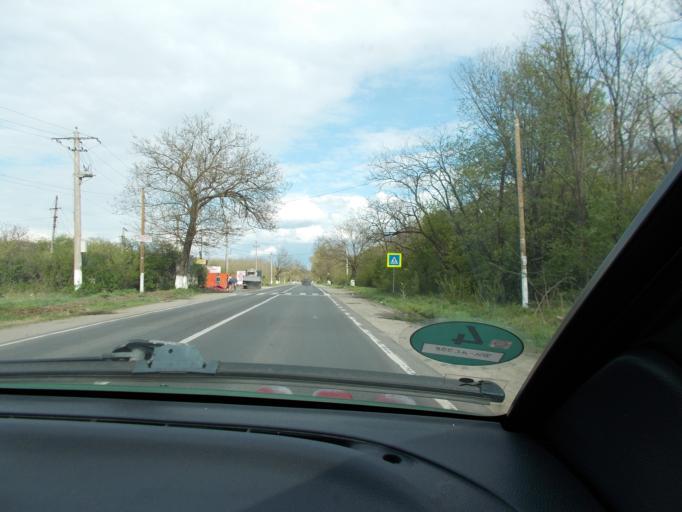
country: RO
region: Ilfov
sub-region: Comuna Ganeasa
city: Ganeasa
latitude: 44.4561
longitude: 26.2837
